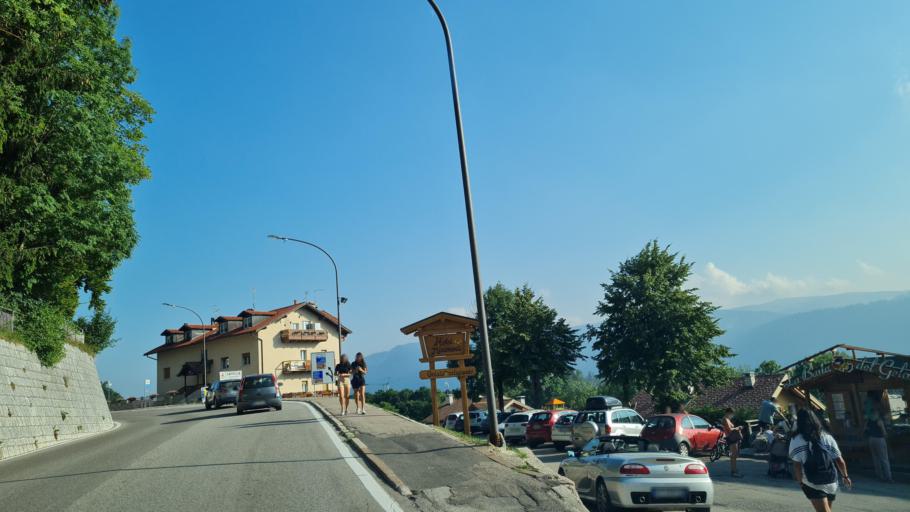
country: IT
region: Trentino-Alto Adige
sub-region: Provincia di Trento
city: Gionghi-Cappella
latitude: 45.9401
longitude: 11.2730
